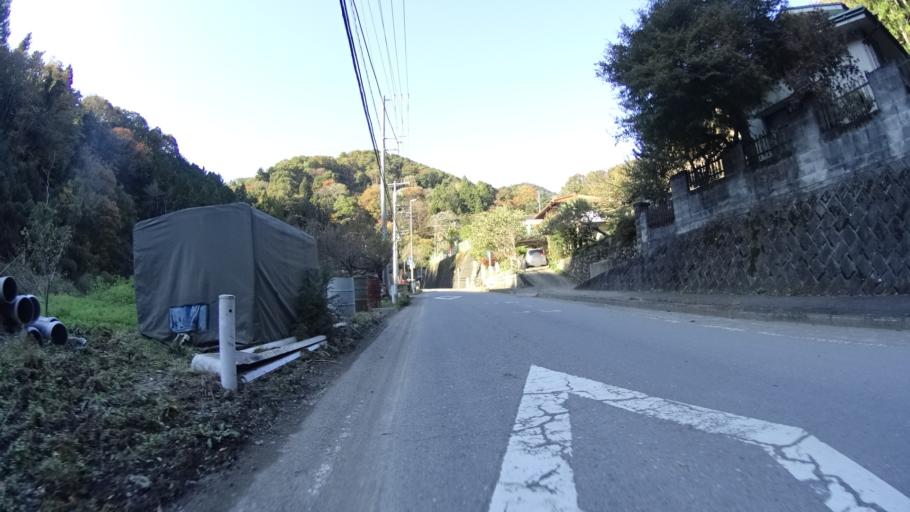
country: JP
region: Yamanashi
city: Uenohara
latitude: 35.6396
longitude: 139.1398
